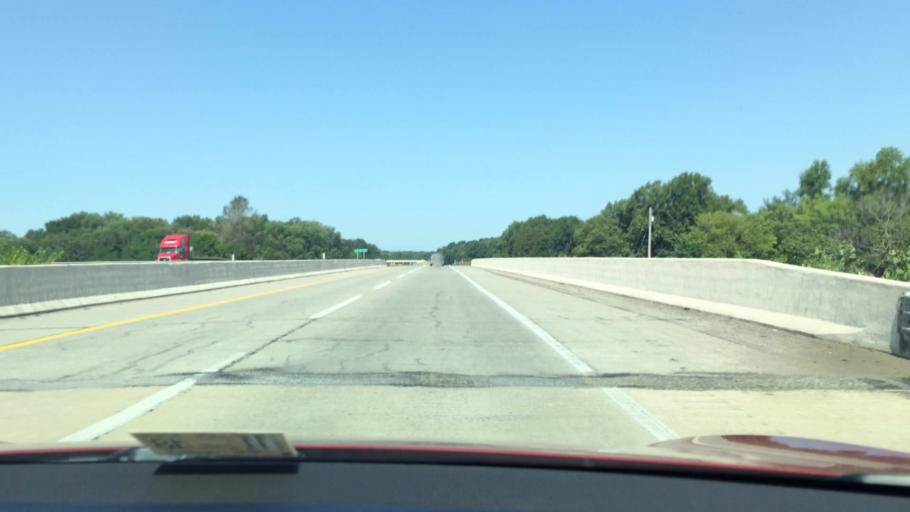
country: US
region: Indiana
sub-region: Elkhart County
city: Bristol
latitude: 41.7347
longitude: -85.8102
